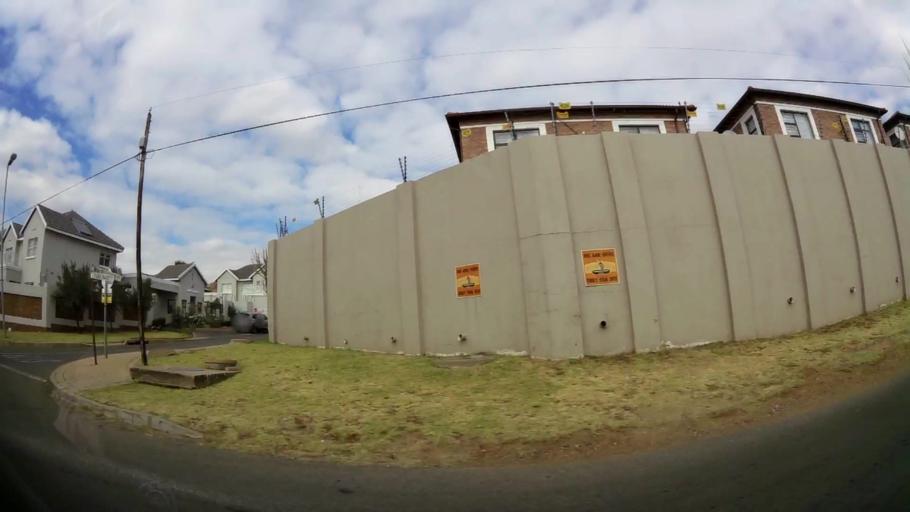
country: ZA
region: Gauteng
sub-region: City of Johannesburg Metropolitan Municipality
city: Roodepoort
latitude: -26.0998
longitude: 27.8737
